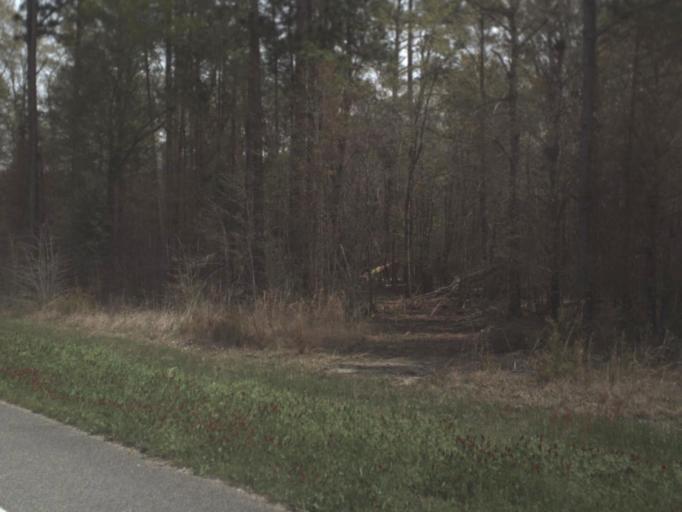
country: US
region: Florida
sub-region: Jackson County
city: Graceville
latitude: 30.9094
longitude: -85.4349
